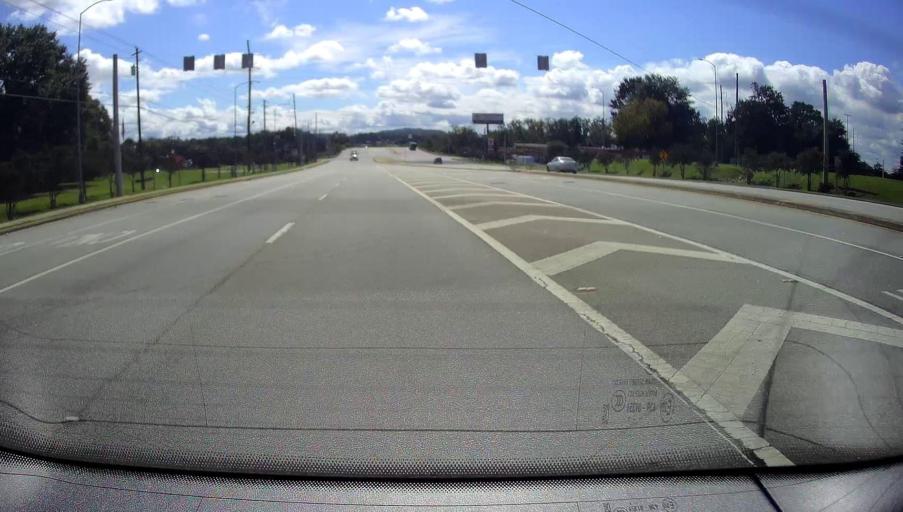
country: US
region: Georgia
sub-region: Bibb County
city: Macon
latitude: 32.8078
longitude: -83.5689
